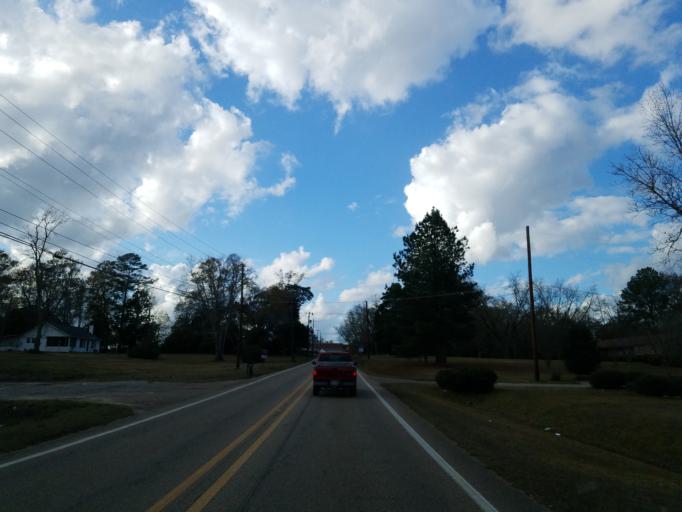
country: US
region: Mississippi
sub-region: Jones County
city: Ellisville
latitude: 31.5951
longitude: -89.1945
